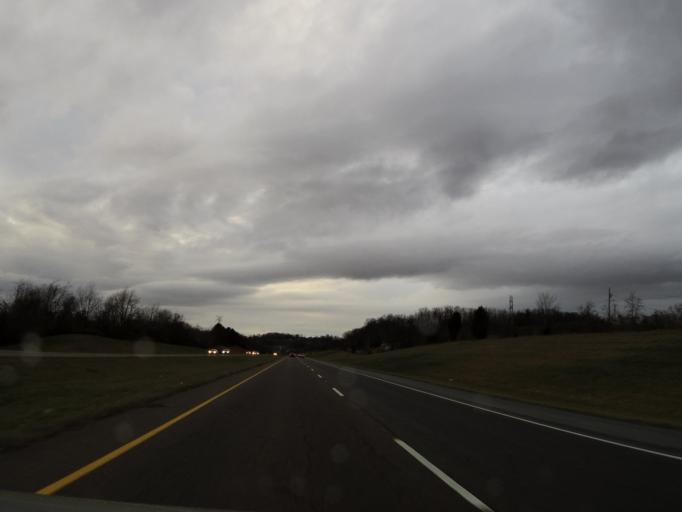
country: US
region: Tennessee
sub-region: Carter County
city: Pine Crest
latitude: 36.3133
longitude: -82.3147
